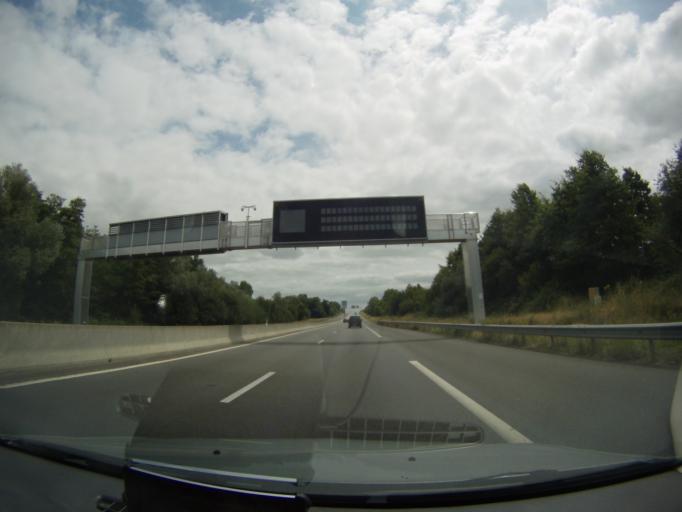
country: FR
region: Pays de la Loire
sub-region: Departement de la Loire-Atlantique
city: Sainte-Luce-sur-Loire
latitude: 47.2415
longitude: -1.4900
